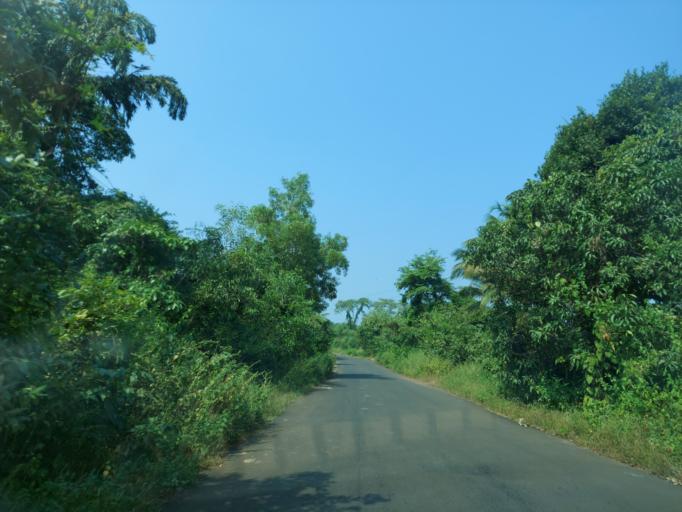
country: IN
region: Maharashtra
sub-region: Sindhudurg
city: Kudal
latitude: 15.9761
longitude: 73.6194
